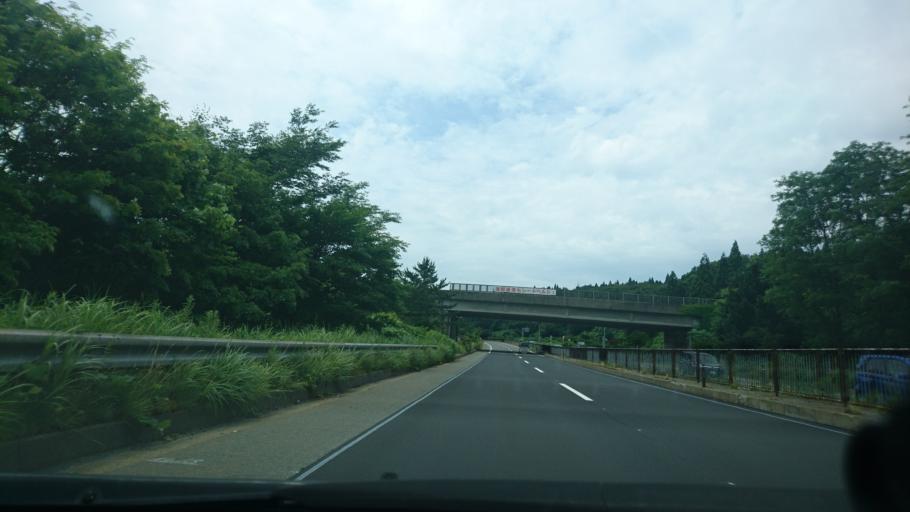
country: JP
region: Akita
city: Akita
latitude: 39.6620
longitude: 140.1884
